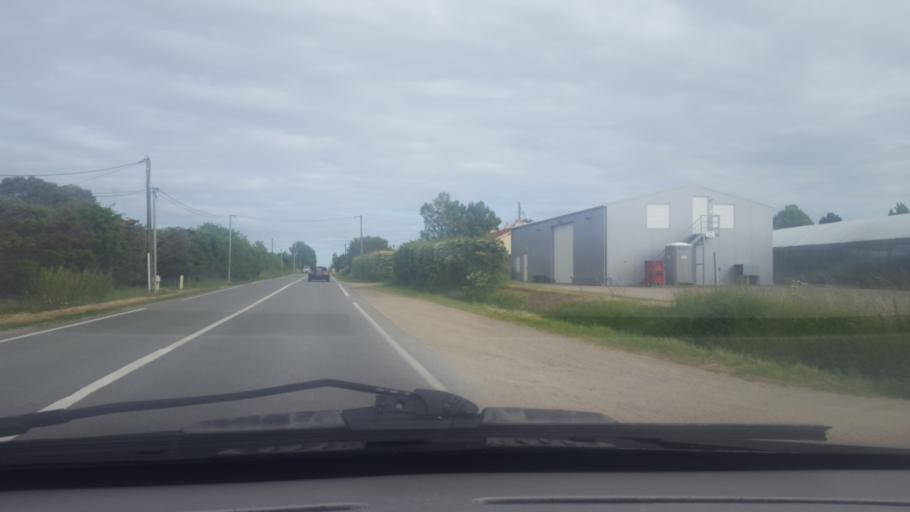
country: FR
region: Pays de la Loire
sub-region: Departement de la Loire-Atlantique
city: Bourgneuf-en-Retz
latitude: 47.0393
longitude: -1.9430
